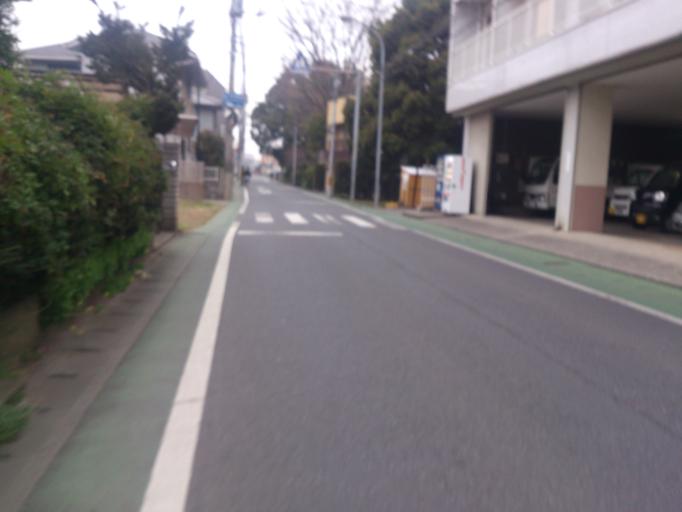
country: JP
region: Chiba
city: Kashiwa
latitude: 35.8038
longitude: 139.9569
